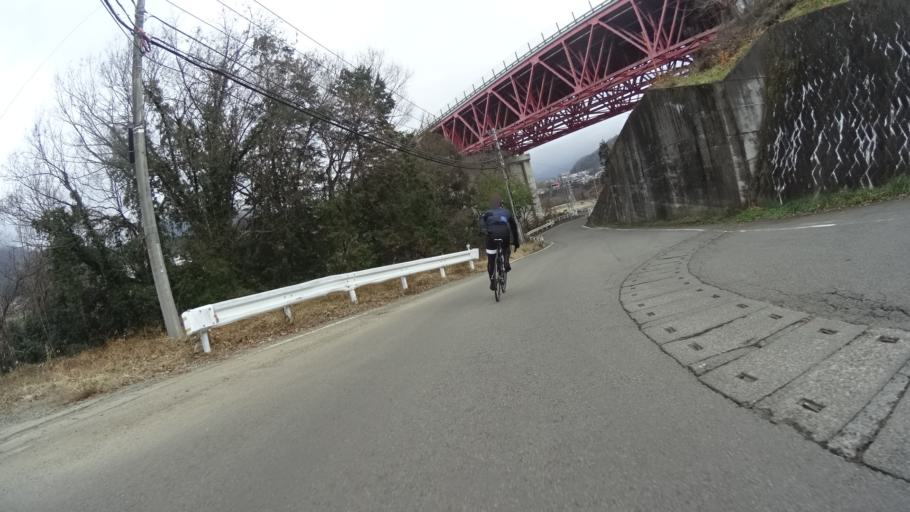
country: JP
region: Yamanashi
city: Otsuki
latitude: 35.6167
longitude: 138.9678
